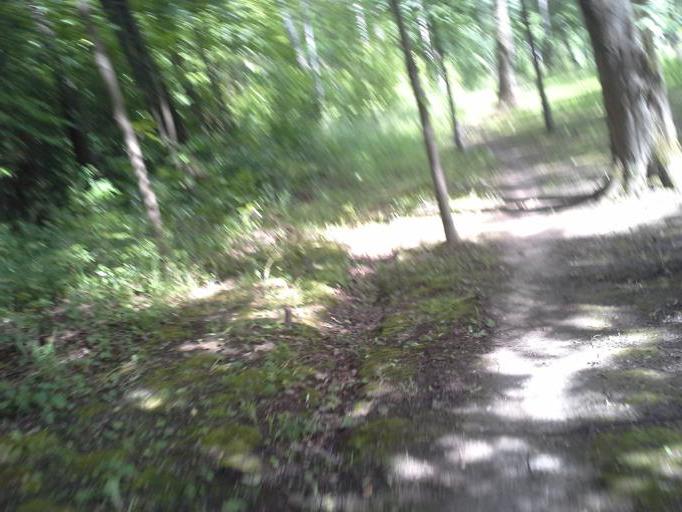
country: RU
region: Moskovskaya
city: Moskovskiy
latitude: 55.5817
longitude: 37.3619
